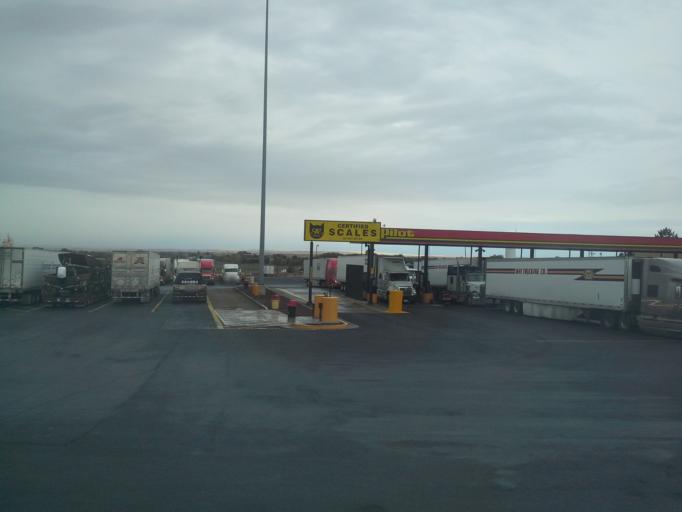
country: US
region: Oregon
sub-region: Umatilla County
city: Stanfield
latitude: 45.7655
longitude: -119.2065
